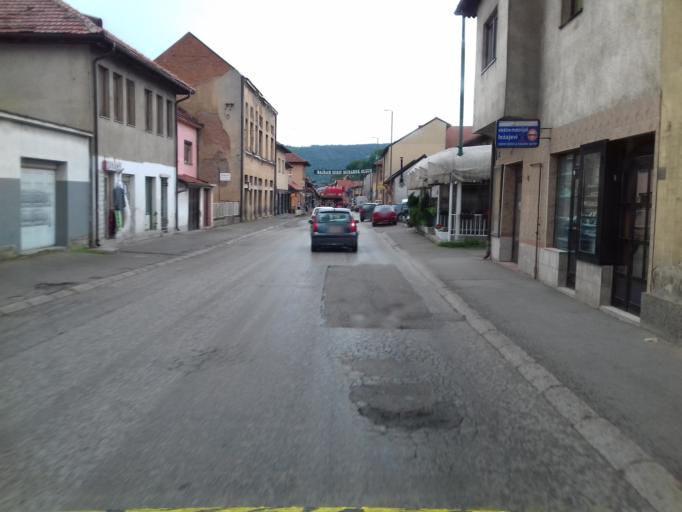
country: BA
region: Federation of Bosnia and Herzegovina
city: Visoko
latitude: 43.9863
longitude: 18.1789
